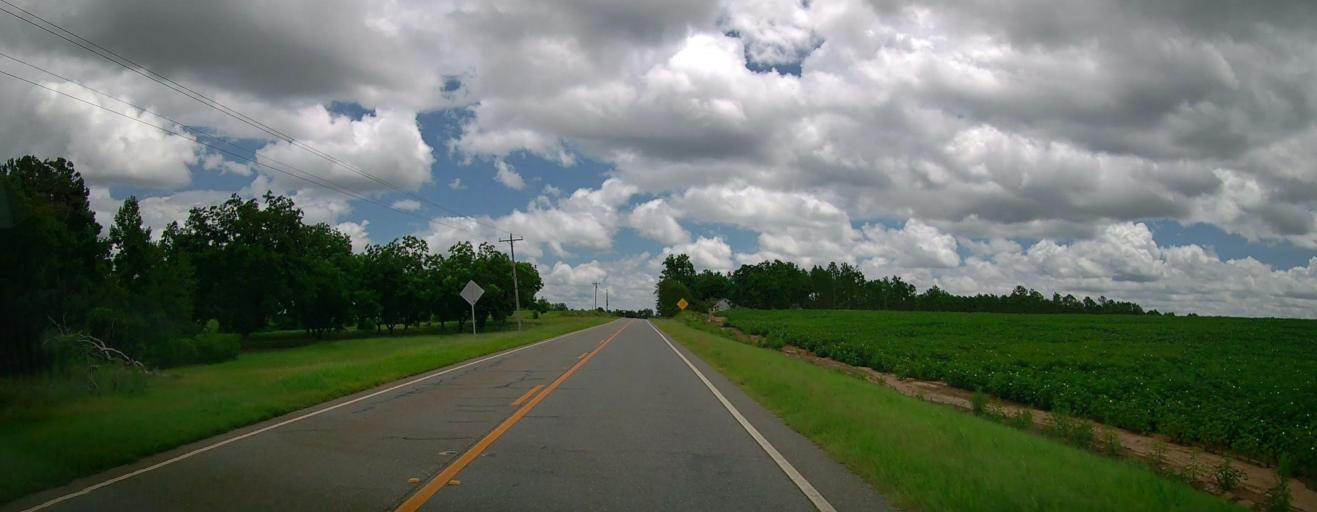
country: US
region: Georgia
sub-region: Wilcox County
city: Rochelle
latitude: 31.9938
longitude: -83.5506
